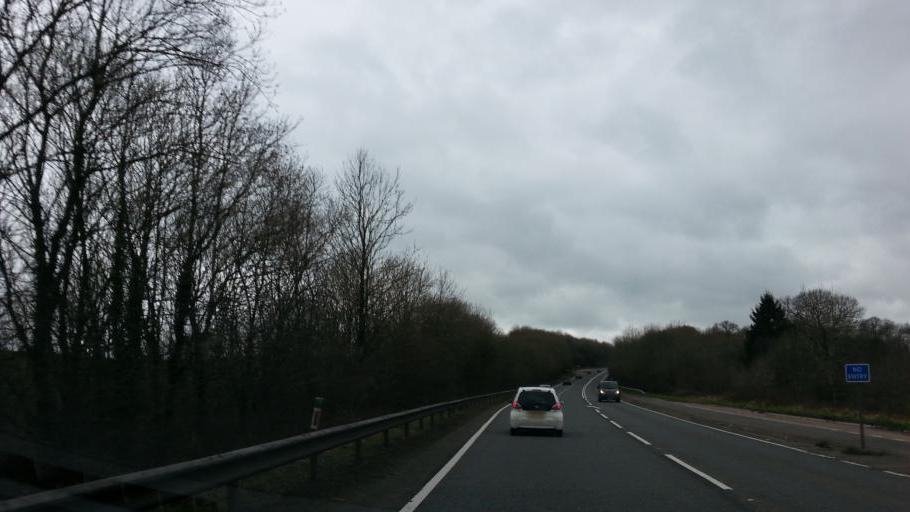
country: GB
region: England
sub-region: Devon
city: South Molton
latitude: 51.0004
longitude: -3.7370
